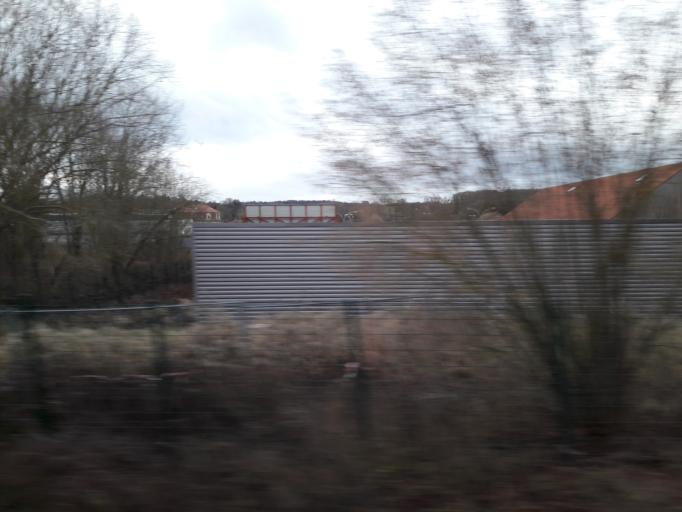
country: FR
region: Franche-Comte
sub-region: Territoire de Belfort
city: Delle
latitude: 47.5155
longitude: 7.0042
